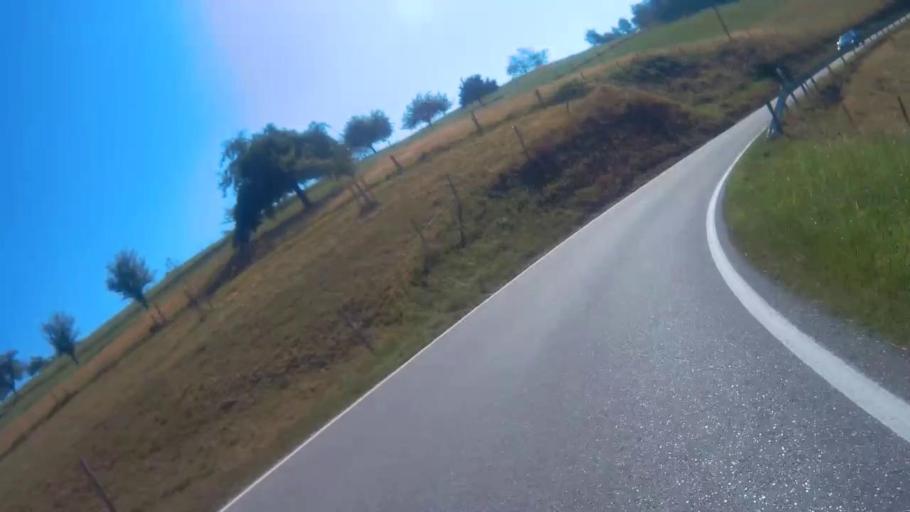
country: DE
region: Baden-Wuerttemberg
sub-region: Freiburg Region
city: Zell im Wiesental
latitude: 47.7168
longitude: 7.8394
